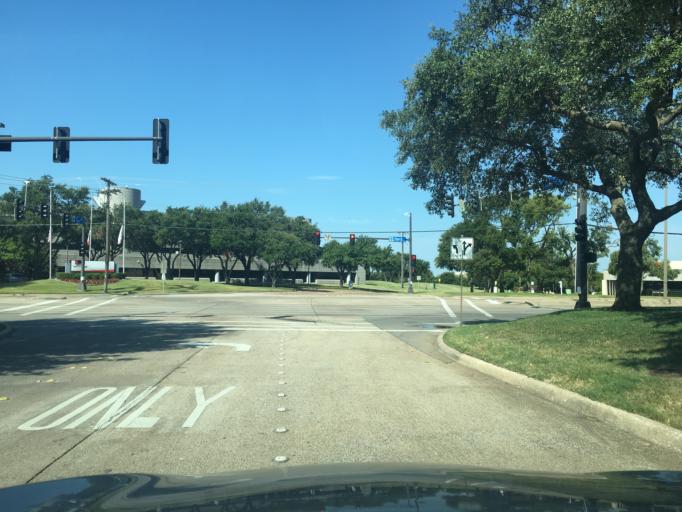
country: US
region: Texas
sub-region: Dallas County
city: Addison
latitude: 32.9653
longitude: -96.8385
